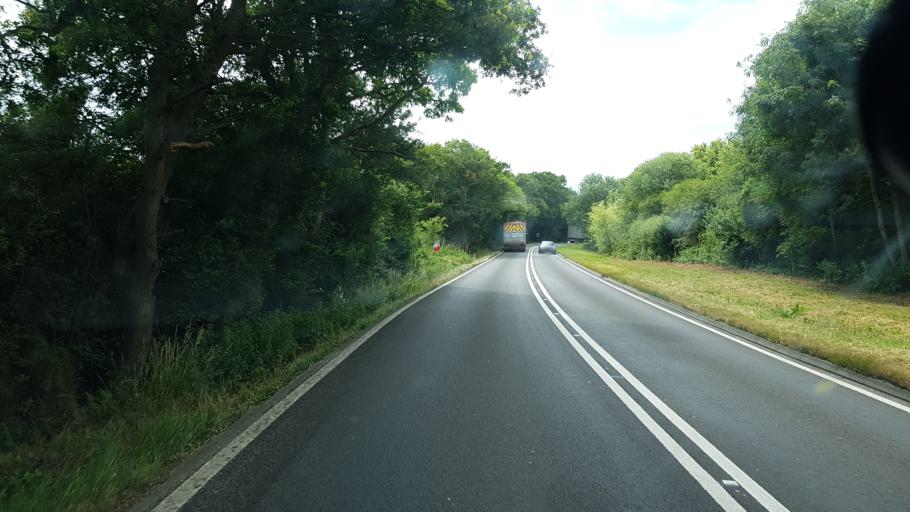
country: GB
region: England
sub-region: Surrey
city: Lingfield
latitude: 51.1793
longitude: -0.0468
